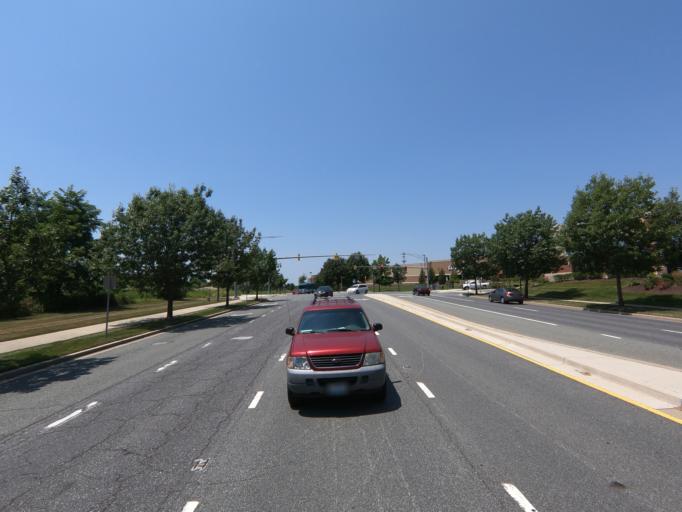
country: US
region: Maryland
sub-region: Montgomery County
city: Germantown
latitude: 39.1982
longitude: -77.2551
